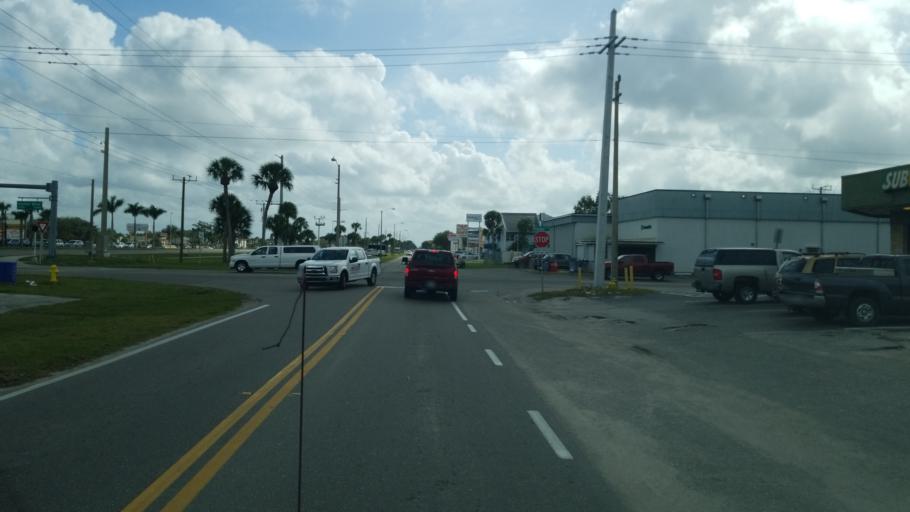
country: US
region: Florida
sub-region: Charlotte County
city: Port Charlotte
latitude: 26.9810
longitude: -82.0982
